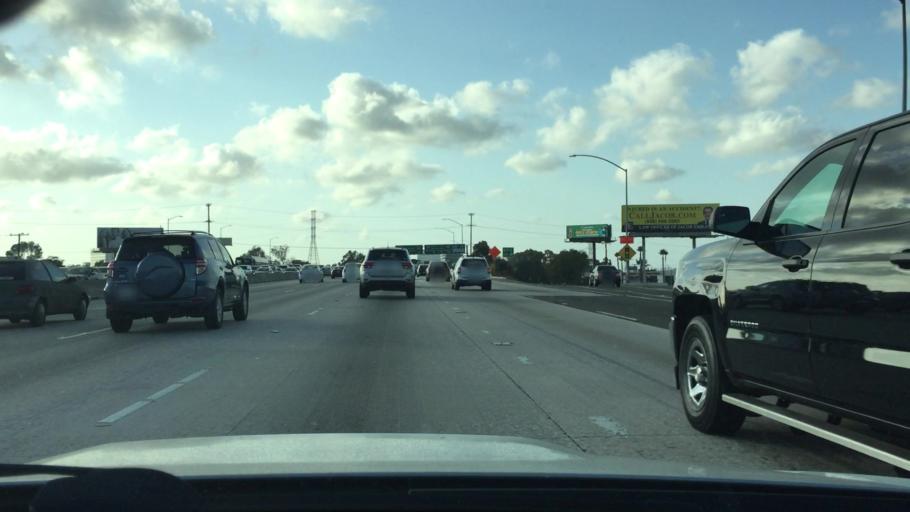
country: US
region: California
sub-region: Los Angeles County
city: Carson
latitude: 33.8518
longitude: -118.2782
